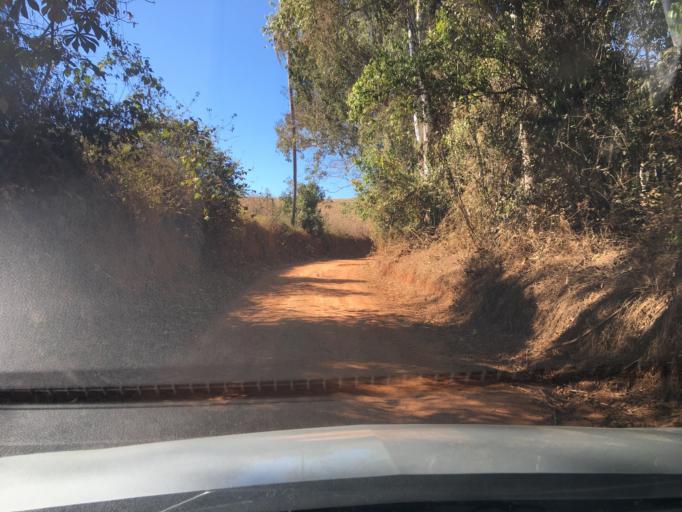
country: BR
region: Minas Gerais
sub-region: Campestre
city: Campestre
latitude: -21.5805
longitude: -46.2036
